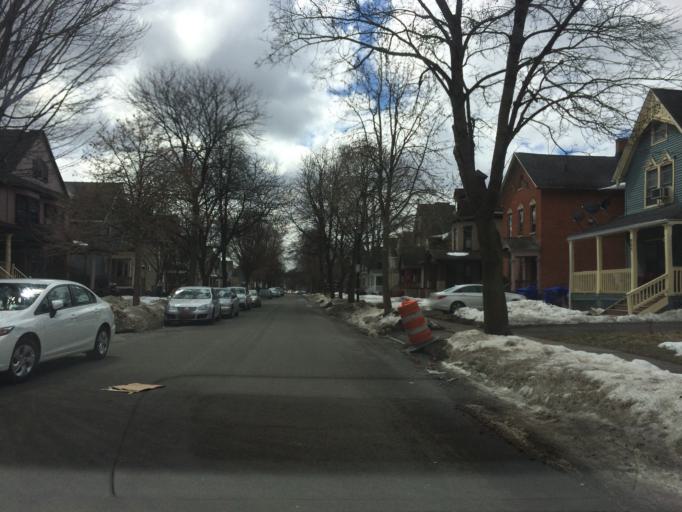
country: US
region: New York
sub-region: Monroe County
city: Rochester
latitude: 43.1492
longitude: -77.5935
